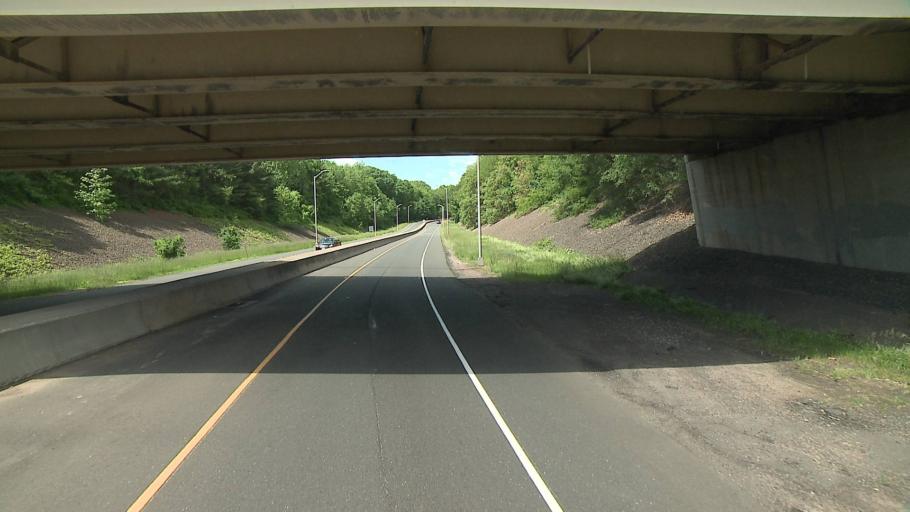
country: US
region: Connecticut
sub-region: Hartford County
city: Blue Hills
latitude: 41.8171
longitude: -72.6711
